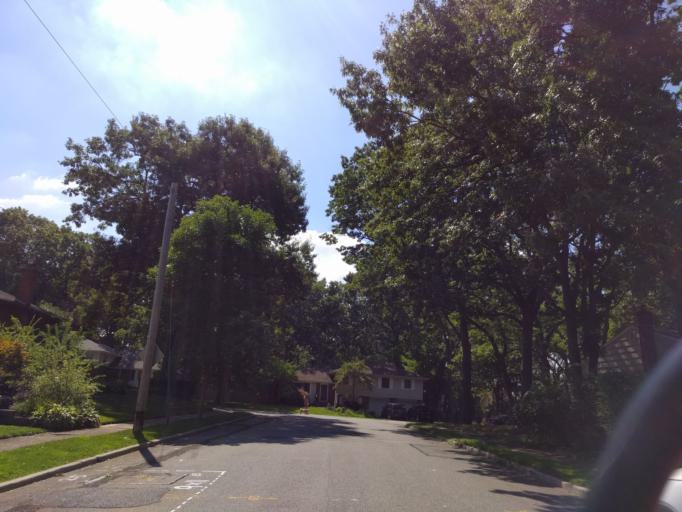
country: US
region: New York
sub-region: Nassau County
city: Oyster Bay
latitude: 40.8585
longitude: -73.5308
